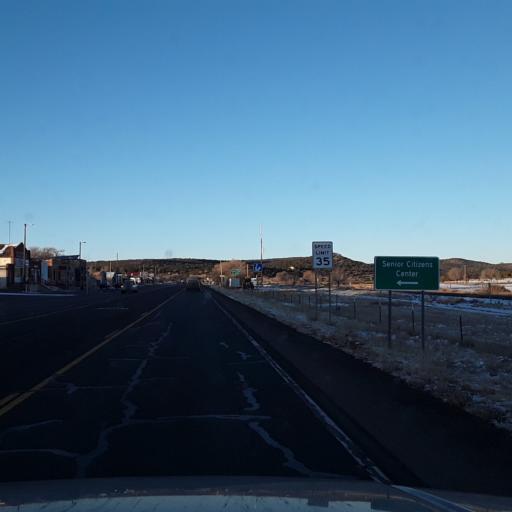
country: US
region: New Mexico
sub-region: Lincoln County
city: Carrizozo
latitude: 34.2477
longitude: -105.5948
